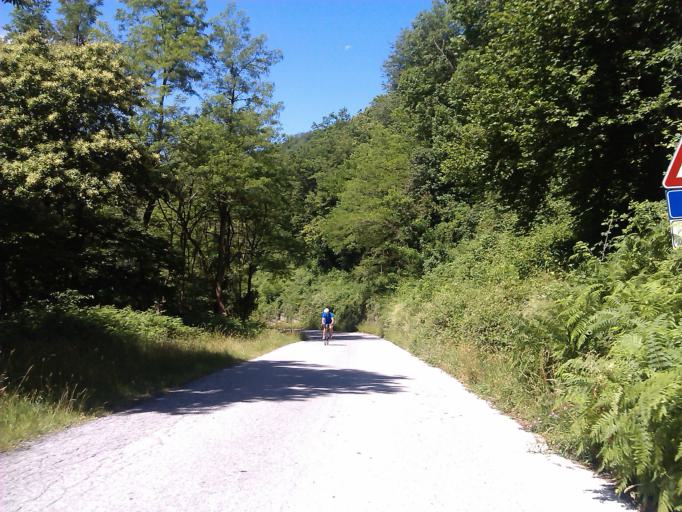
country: IT
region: Tuscany
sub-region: Provincia di Pistoia
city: Sambuca Pistoiese
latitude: 44.0858
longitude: 11.0453
